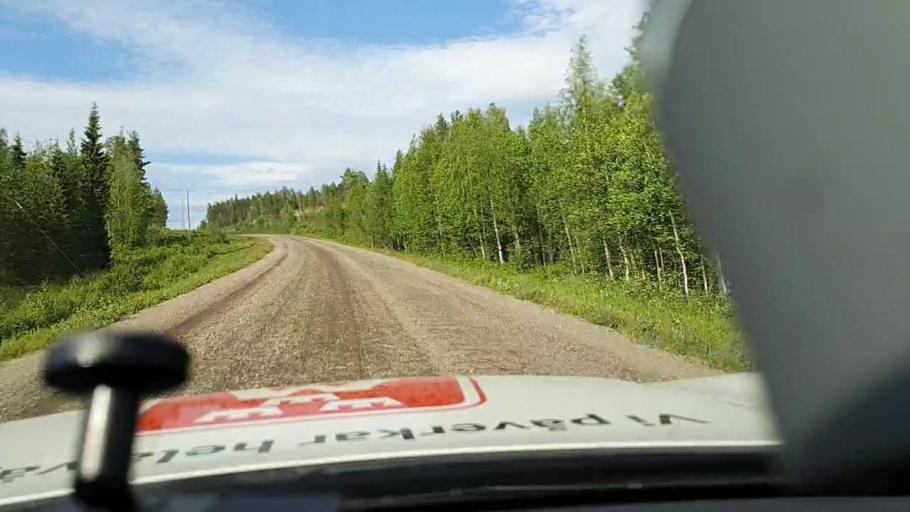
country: SE
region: Norrbotten
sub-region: Alvsbyns Kommun
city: AElvsbyn
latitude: 66.1651
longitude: 21.0557
